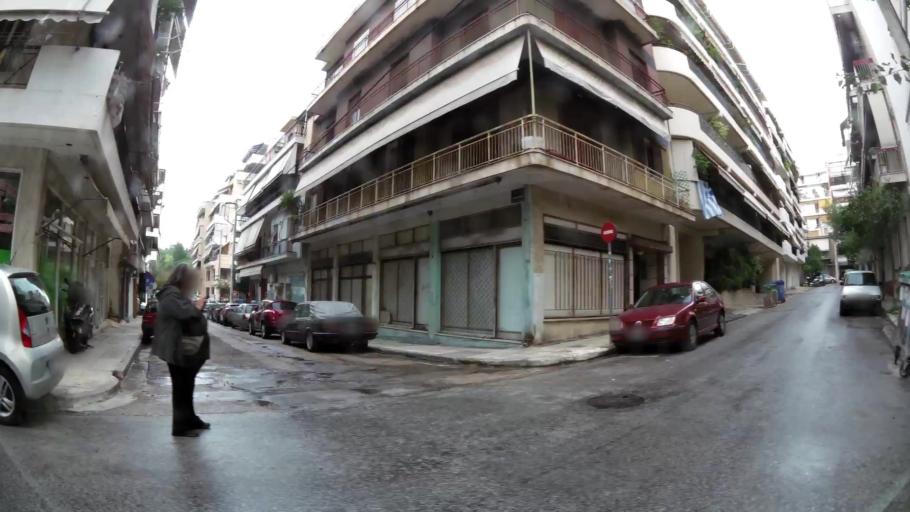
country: GR
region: Attica
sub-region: Nomarchia Athinas
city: Kaisariani
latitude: 37.9663
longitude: 23.7670
